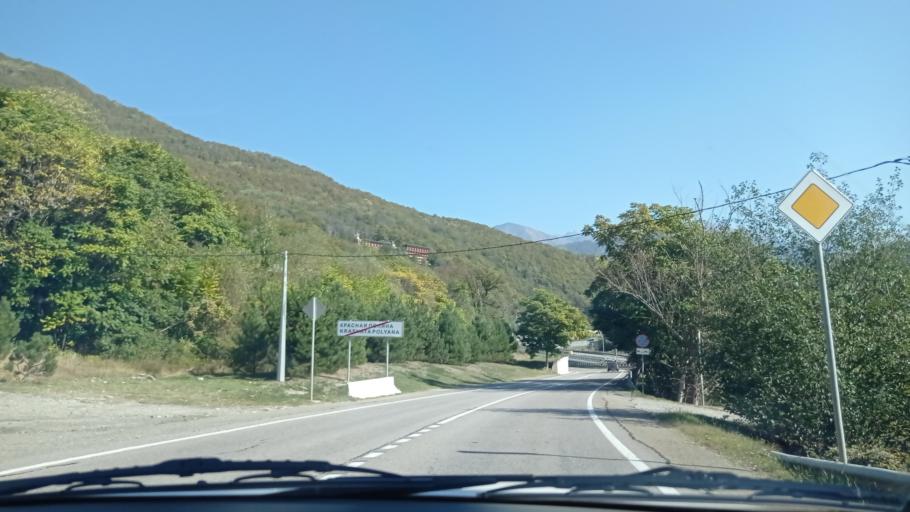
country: RU
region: Krasnodarskiy
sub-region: Sochi City
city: Krasnaya Polyana
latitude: 43.6850
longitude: 40.2284
